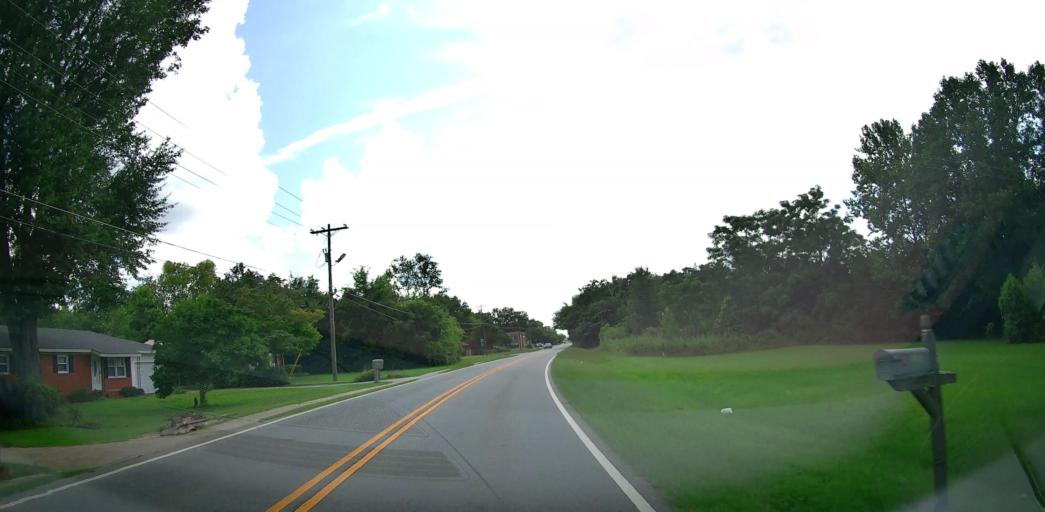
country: US
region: Georgia
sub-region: Houston County
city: Warner Robins
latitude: 32.6333
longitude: -83.6355
